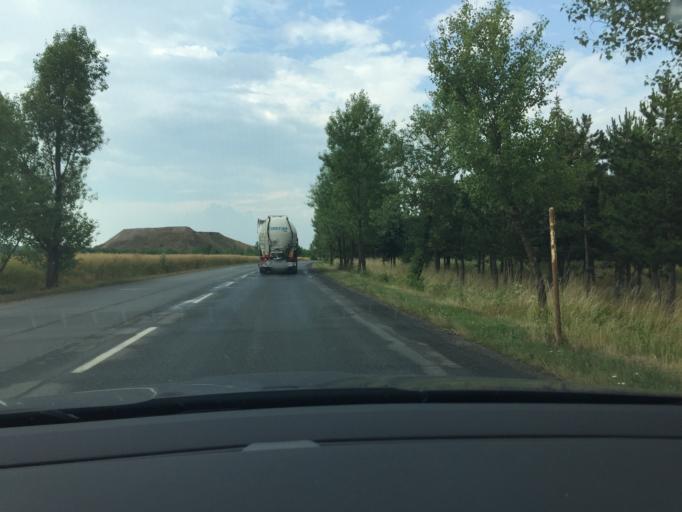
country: CZ
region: Central Bohemia
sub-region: Okres Melnik
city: Veltrusy
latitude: 50.2571
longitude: 14.3185
